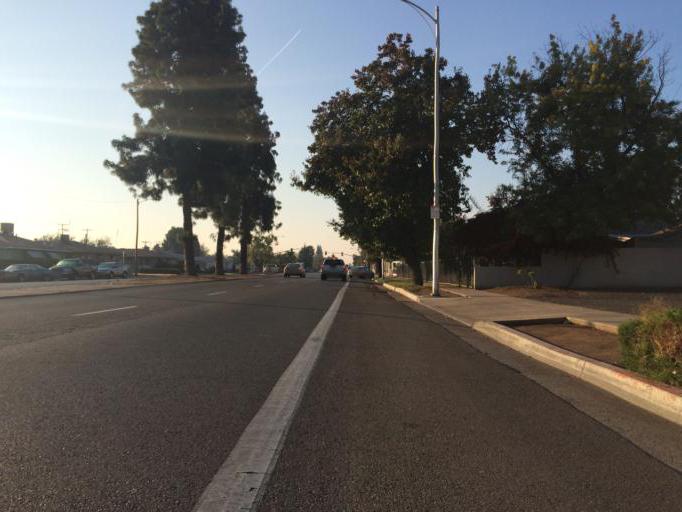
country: US
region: California
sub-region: Fresno County
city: Fresno
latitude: 36.7739
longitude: -119.7727
